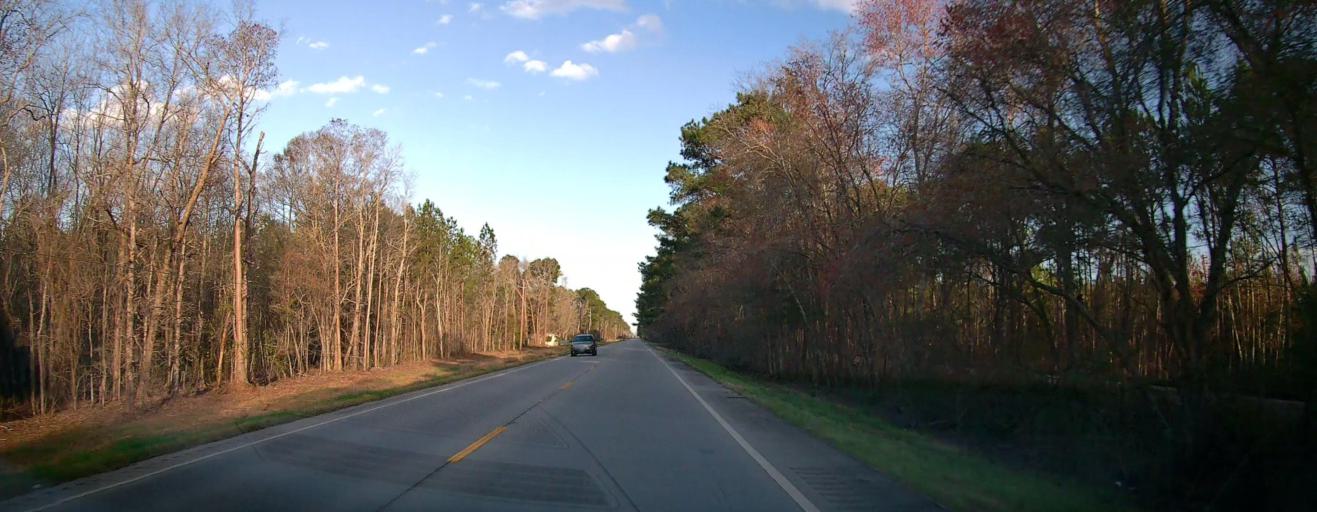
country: US
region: Georgia
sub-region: Bryan County
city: Pembroke
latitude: 32.1384
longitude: -81.6612
